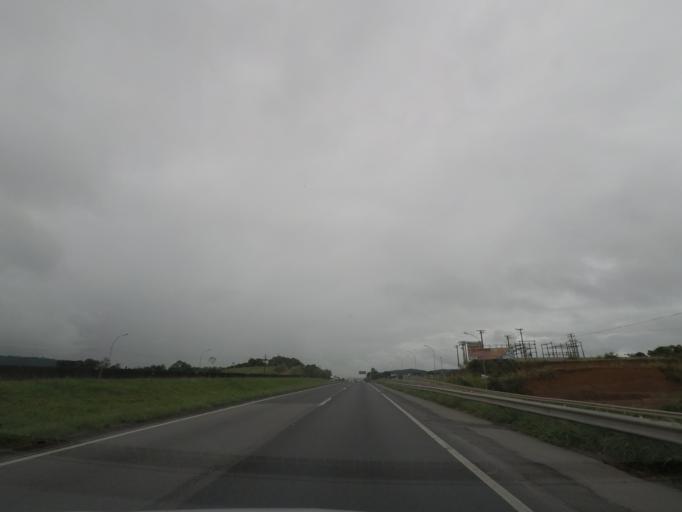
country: BR
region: Sao Paulo
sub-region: Jacupiranga
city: Jacupiranga
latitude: -24.7086
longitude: -48.0172
